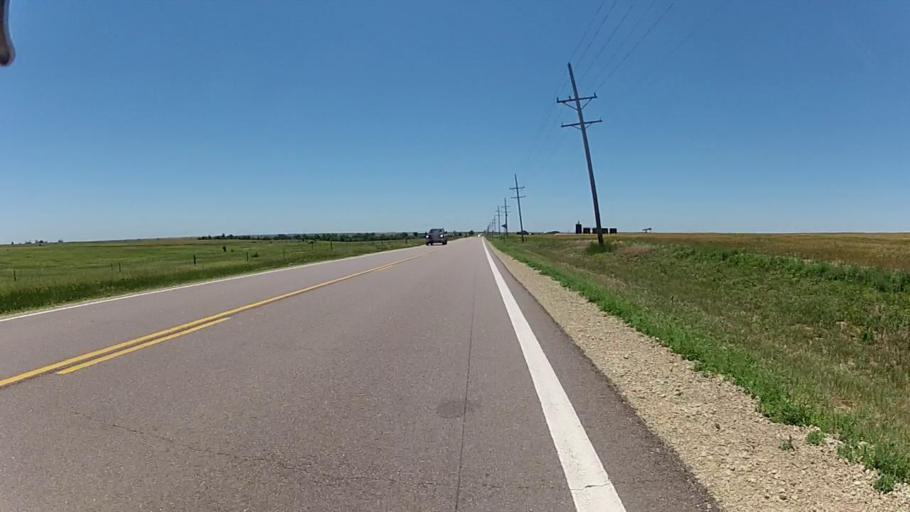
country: US
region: Kansas
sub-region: Kiowa County
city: Greensburg
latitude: 37.5109
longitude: -99.3204
